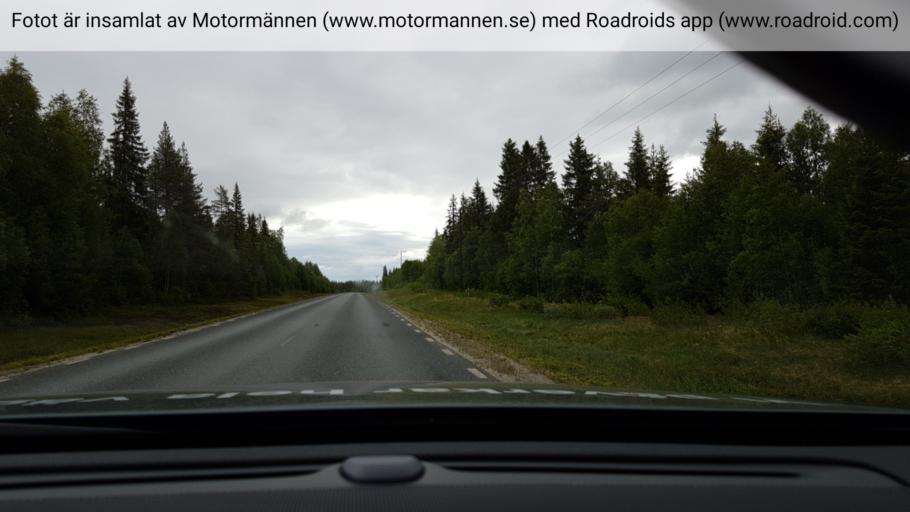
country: SE
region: Vaesterbotten
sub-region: Lycksele Kommun
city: Soderfors
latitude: 64.4727
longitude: 18.1992
